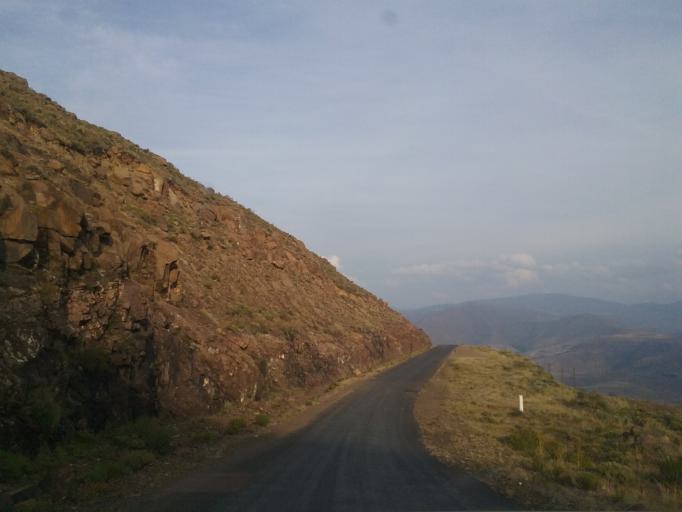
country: LS
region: Quthing
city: Quthing
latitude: -30.1909
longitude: 27.9670
